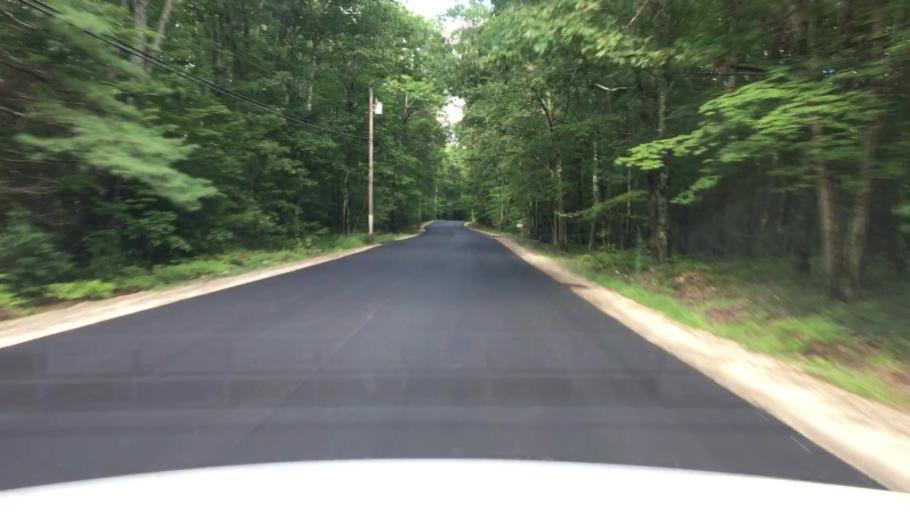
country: US
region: Maine
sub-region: York County
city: West Kennebunk
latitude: 43.4372
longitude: -70.6359
